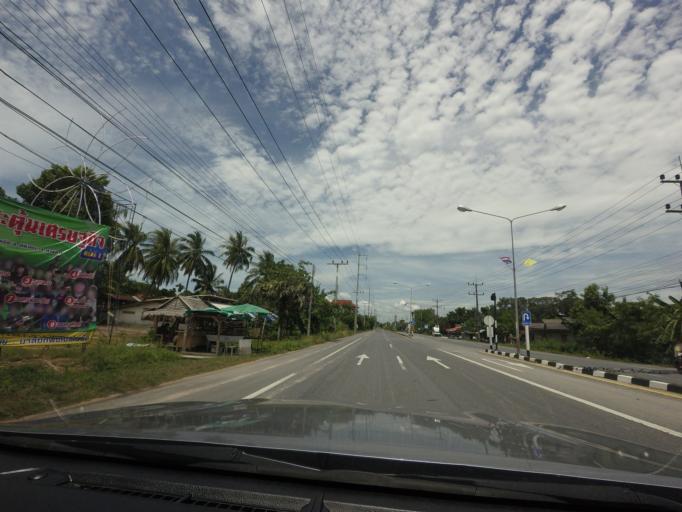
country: TH
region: Songkhla
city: Sathing Phra
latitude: 7.5633
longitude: 100.4122
